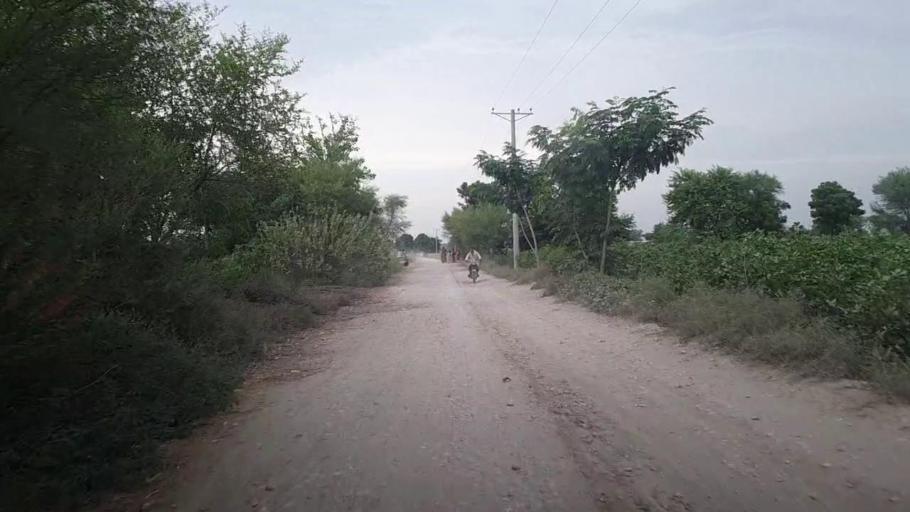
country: PK
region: Sindh
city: Karaundi
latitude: 26.9783
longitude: 68.3438
